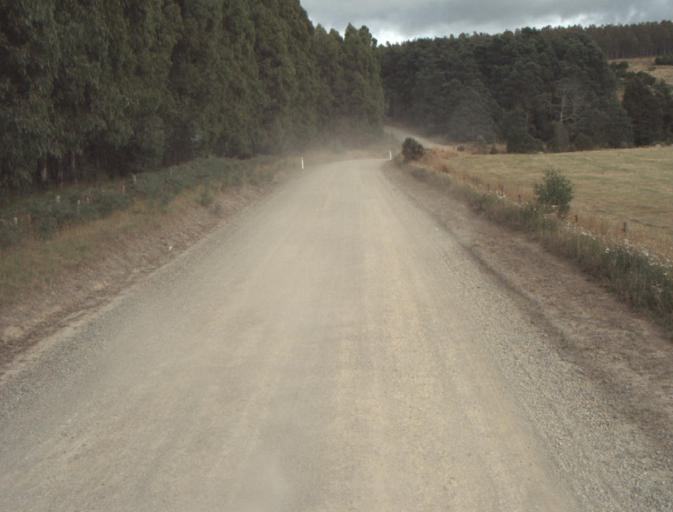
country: AU
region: Tasmania
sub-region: Dorset
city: Scottsdale
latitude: -41.3445
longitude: 147.4369
